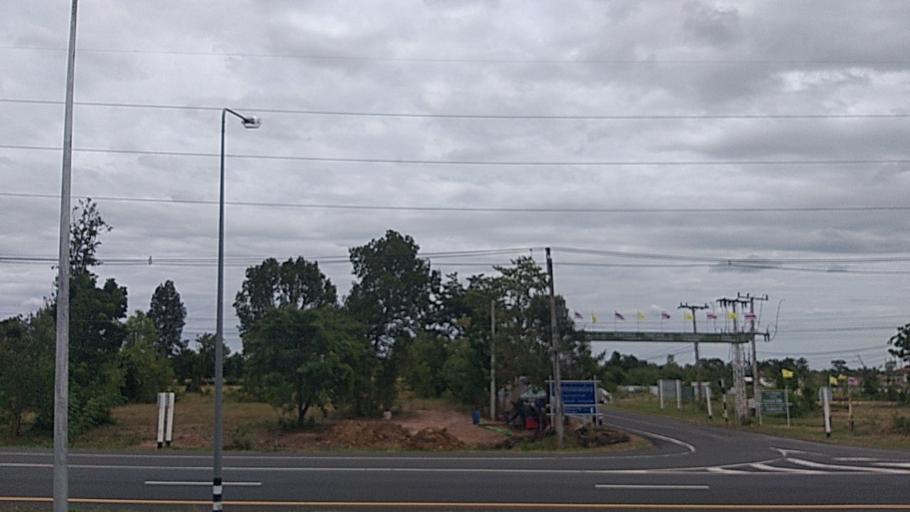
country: TH
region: Buriram
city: Chaloem Phra Kiat
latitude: 14.6069
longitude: 102.9702
